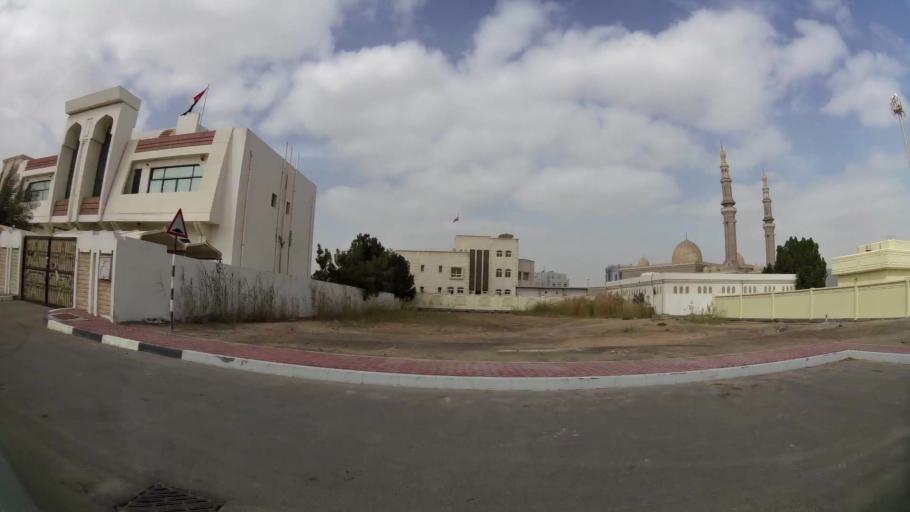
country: AE
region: Abu Dhabi
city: Abu Dhabi
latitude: 24.4051
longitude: 54.5068
